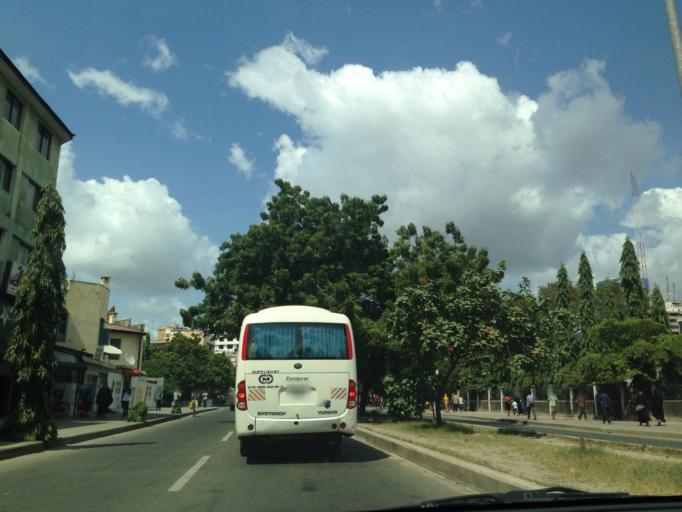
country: TZ
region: Dar es Salaam
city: Dar es Salaam
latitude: -6.8189
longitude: 39.2806
